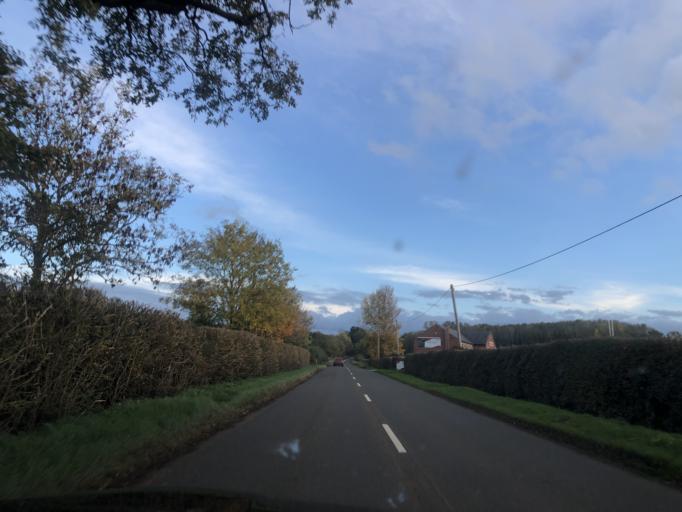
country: GB
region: England
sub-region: Warwickshire
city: Harbury
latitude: 52.2413
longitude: -1.4752
